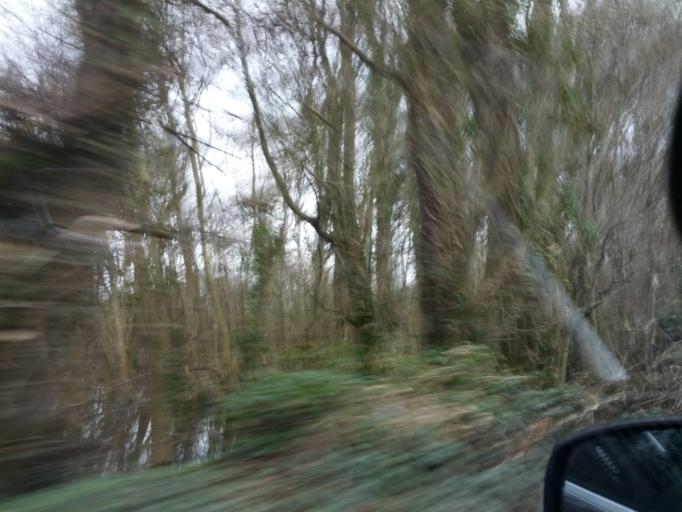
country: IE
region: Connaught
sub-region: County Galway
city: Oranmore
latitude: 53.1790
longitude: -8.9006
